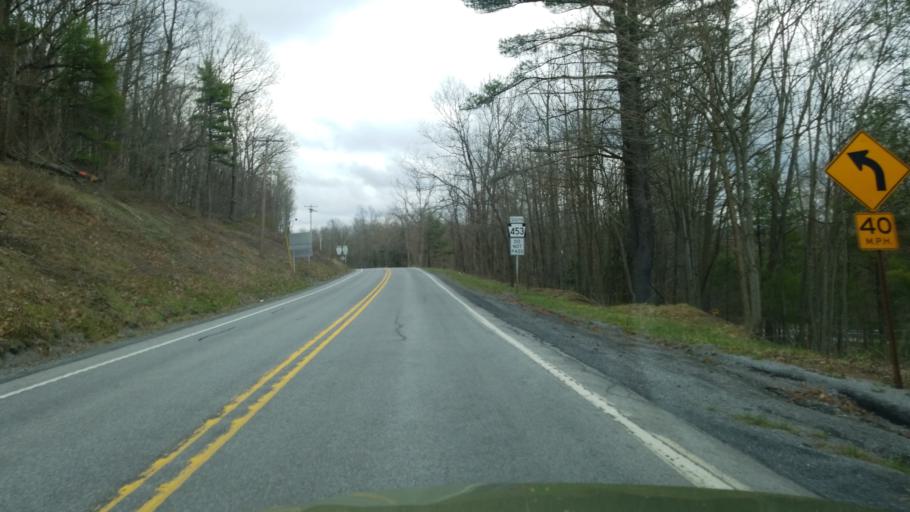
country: US
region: Pennsylvania
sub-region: Blair County
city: Tipton
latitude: 40.7468
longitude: -78.3953
